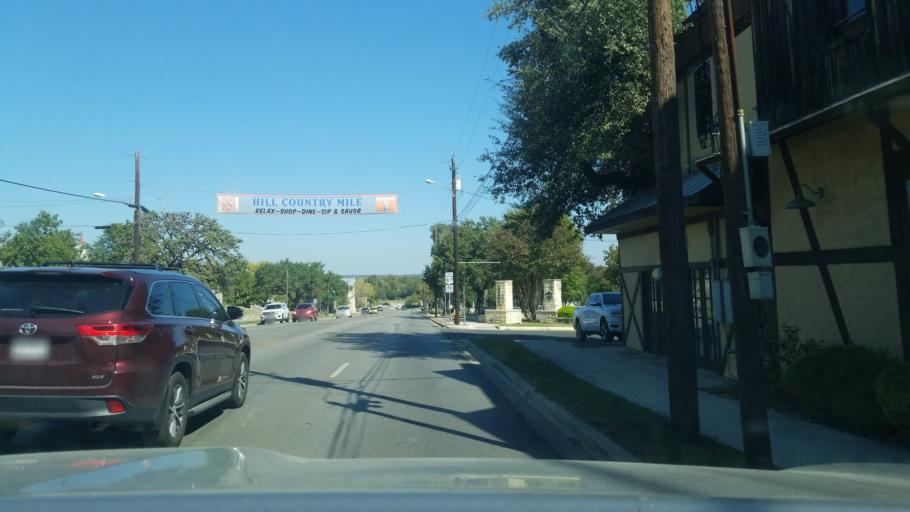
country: US
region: Texas
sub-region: Kendall County
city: Boerne
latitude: 29.7850
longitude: -98.7290
